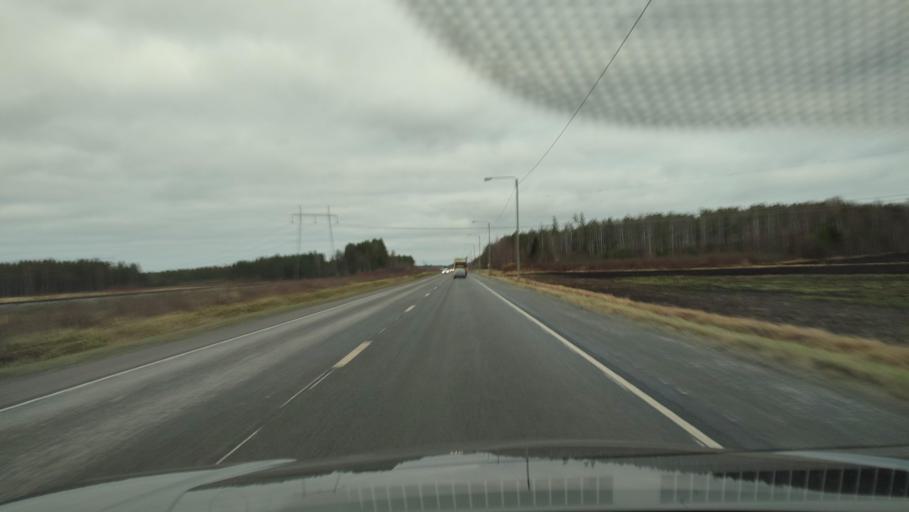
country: FI
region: Southern Ostrobothnia
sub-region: Seinaejoki
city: Ilmajoki
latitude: 62.7451
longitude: 22.6310
